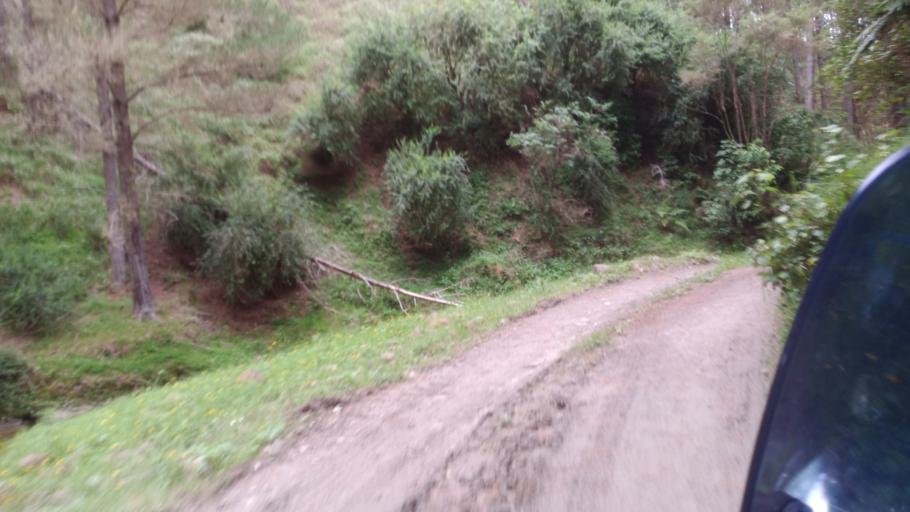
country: NZ
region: Gisborne
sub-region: Gisborne District
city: Gisborne
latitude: -38.4572
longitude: 177.9278
